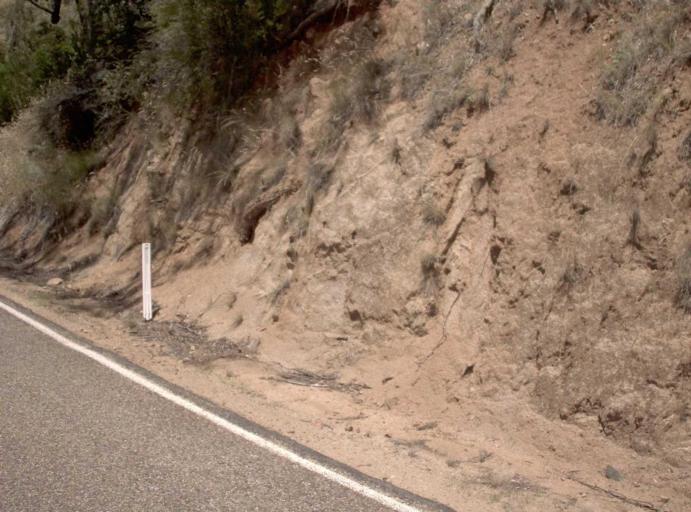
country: AU
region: Victoria
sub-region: East Gippsland
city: Bairnsdale
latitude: -37.3893
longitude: 147.8284
